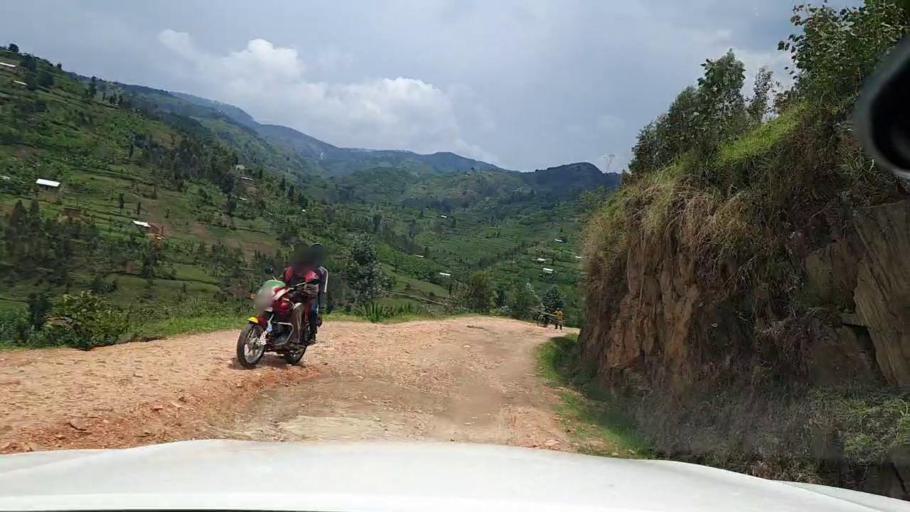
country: RW
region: Western Province
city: Kibuye
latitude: -2.0719
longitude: 29.4314
